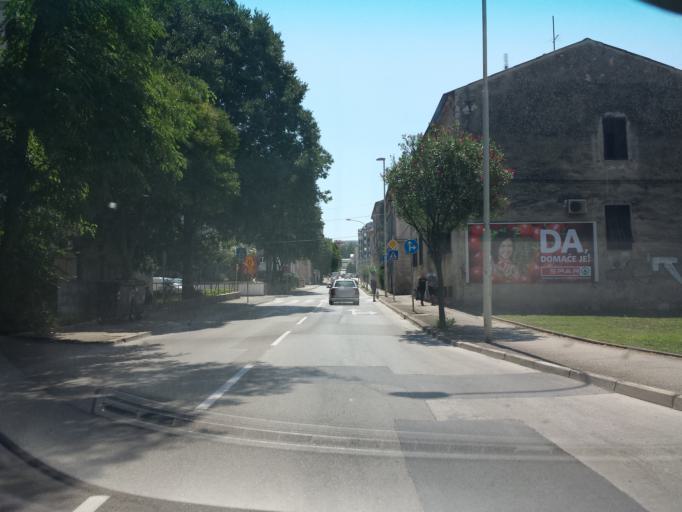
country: HR
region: Istarska
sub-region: Grad Pula
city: Pula
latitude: 44.8625
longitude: 13.8484
